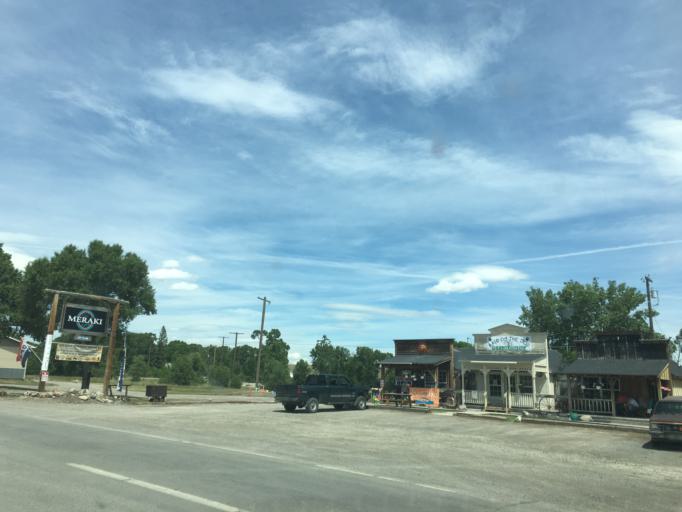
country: US
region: Montana
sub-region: Teton County
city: Choteau
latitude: 47.8193
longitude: -112.1888
